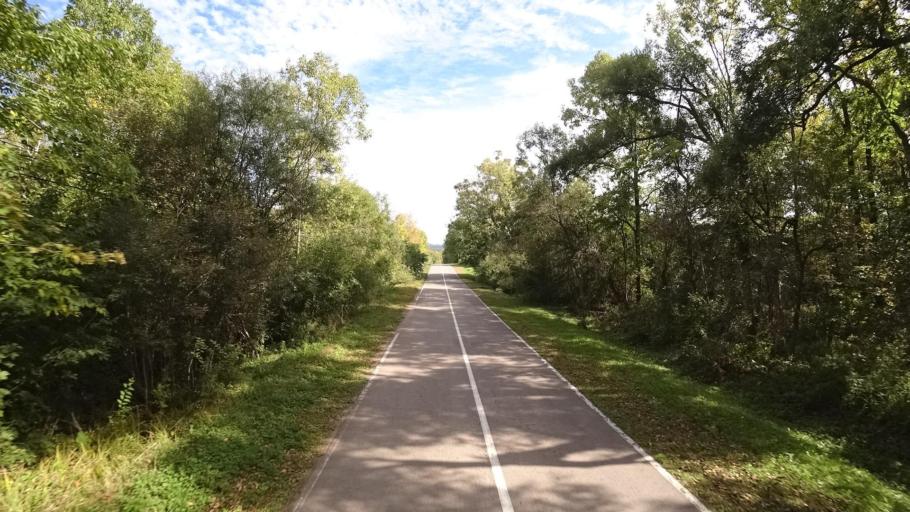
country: RU
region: Primorskiy
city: Yakovlevka
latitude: 44.3955
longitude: 133.6041
